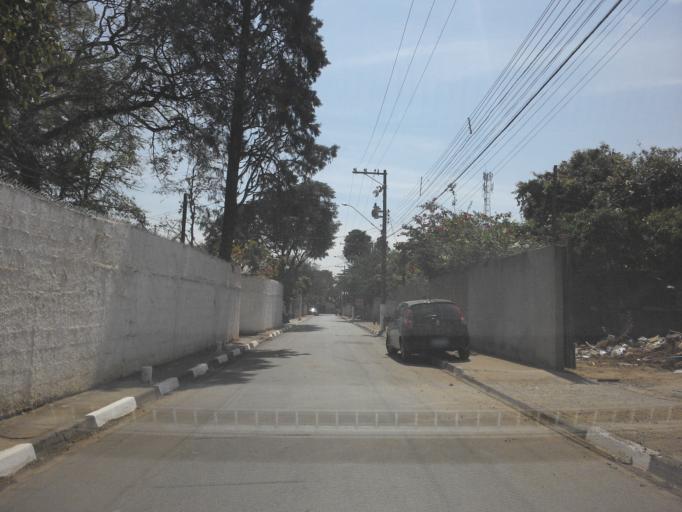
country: BR
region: Sao Paulo
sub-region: Hortolandia
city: Hortolandia
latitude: -22.8992
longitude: -47.2288
